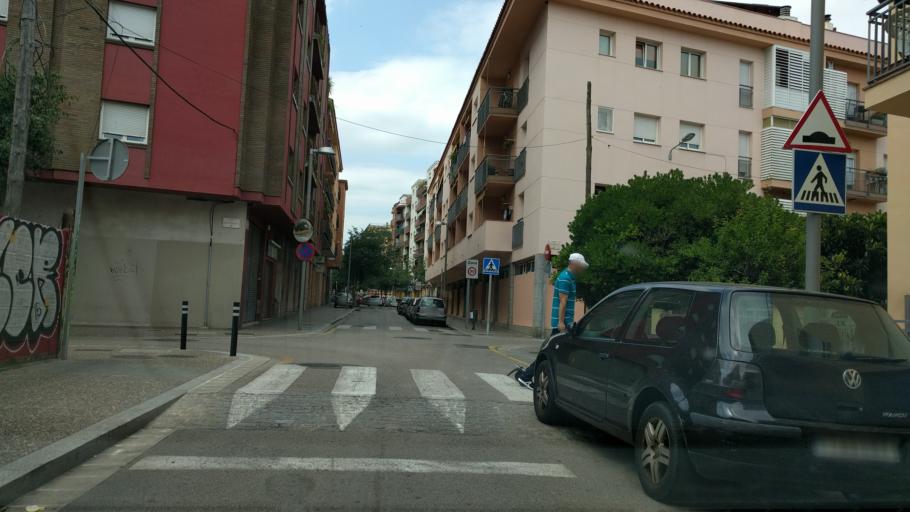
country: ES
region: Catalonia
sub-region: Provincia de Girona
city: Salt
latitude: 41.9768
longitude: 2.8066
